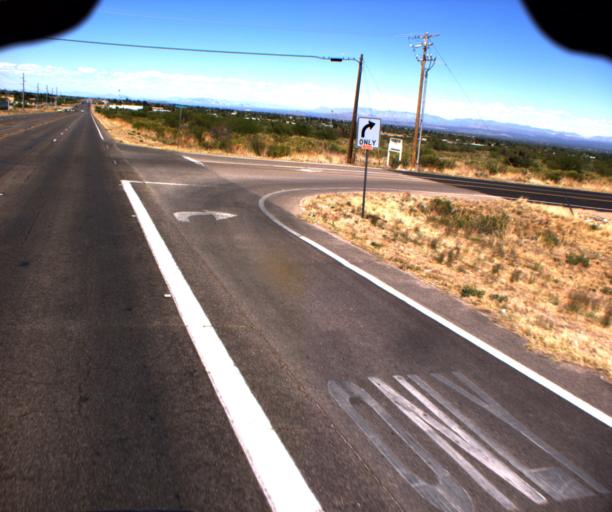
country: US
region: Arizona
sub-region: Cochise County
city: Sierra Vista Southeast
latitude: 31.4592
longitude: -110.2573
